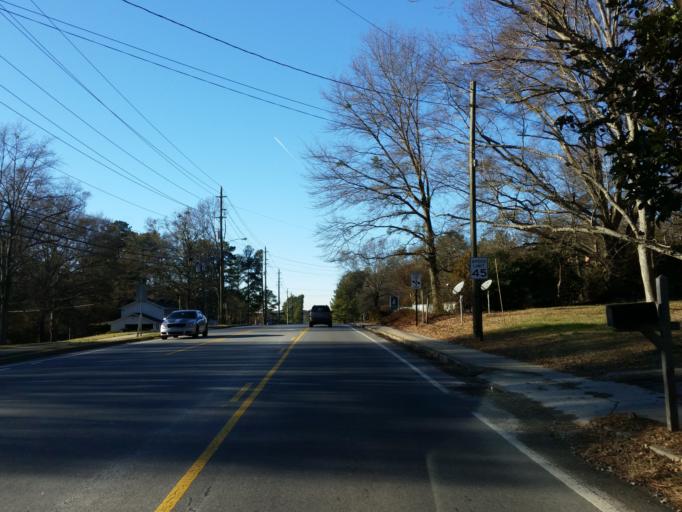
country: US
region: Georgia
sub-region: Cobb County
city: Kennesaw
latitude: 33.9640
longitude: -84.6612
